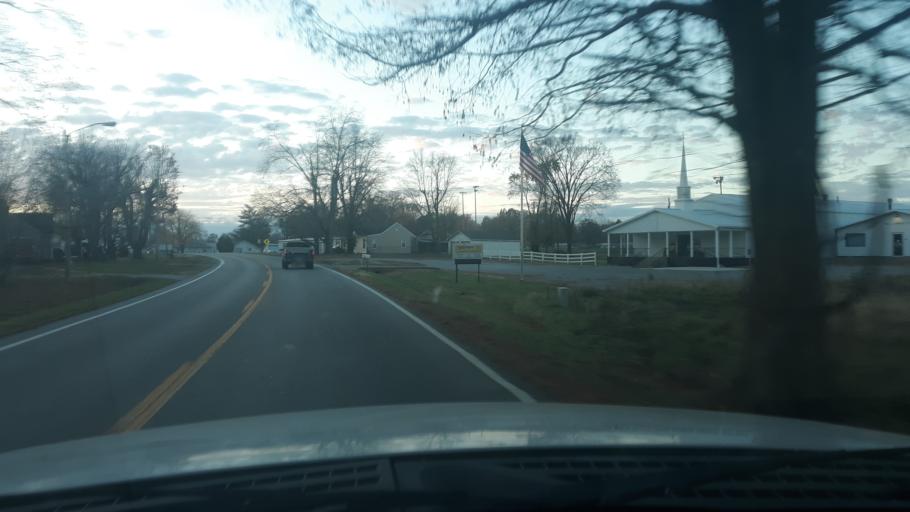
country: US
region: Illinois
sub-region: Saline County
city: Harrisburg
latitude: 37.8404
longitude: -88.6028
